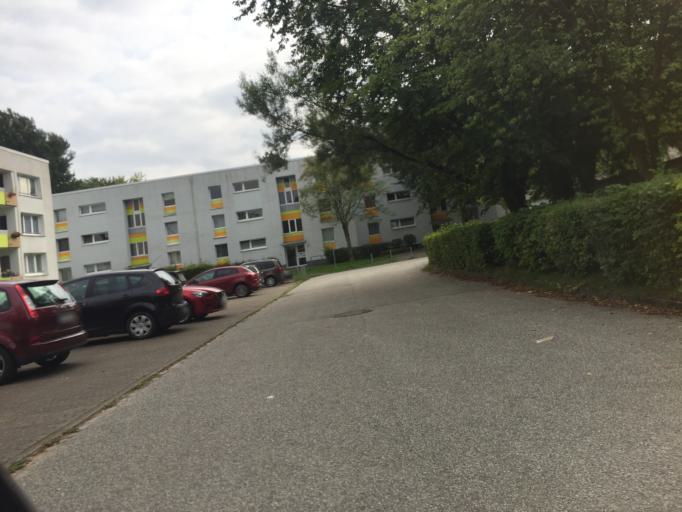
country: DE
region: Schleswig-Holstein
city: Ottenbuttel
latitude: 53.9495
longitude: 9.5071
